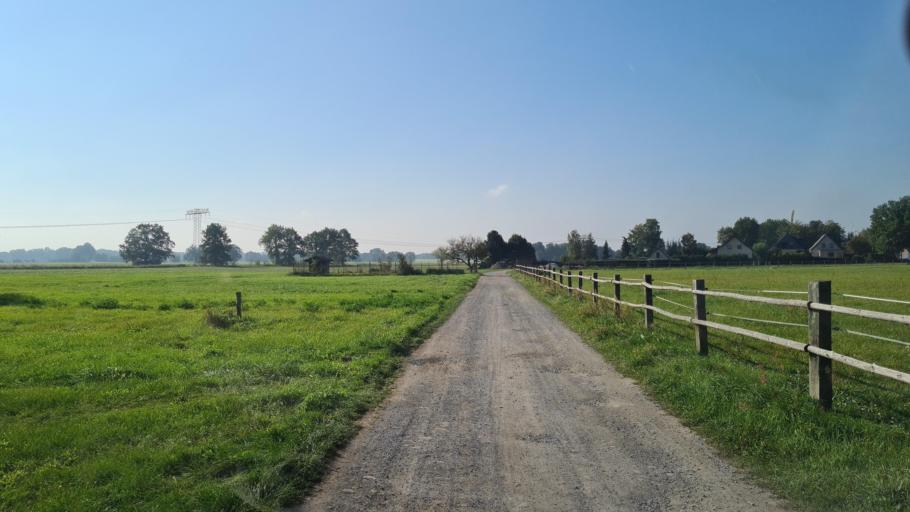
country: DE
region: Brandenburg
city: Luckau
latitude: 51.8448
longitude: 13.7035
